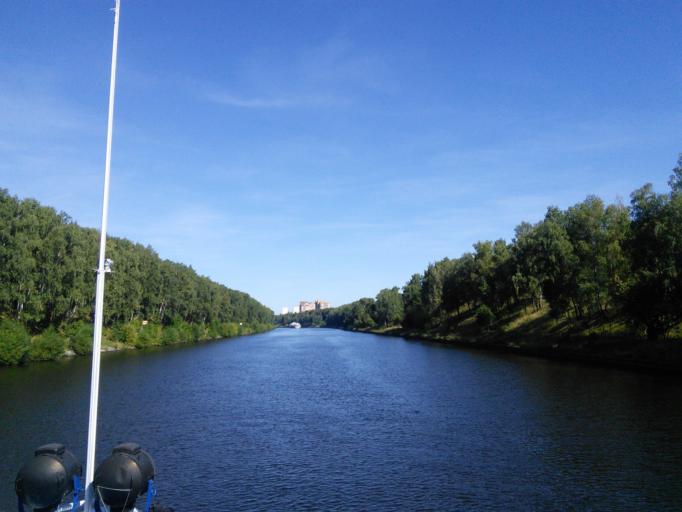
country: RU
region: Moskovskaya
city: Dolgoprudnyy
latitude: 55.9211
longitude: 37.4885
